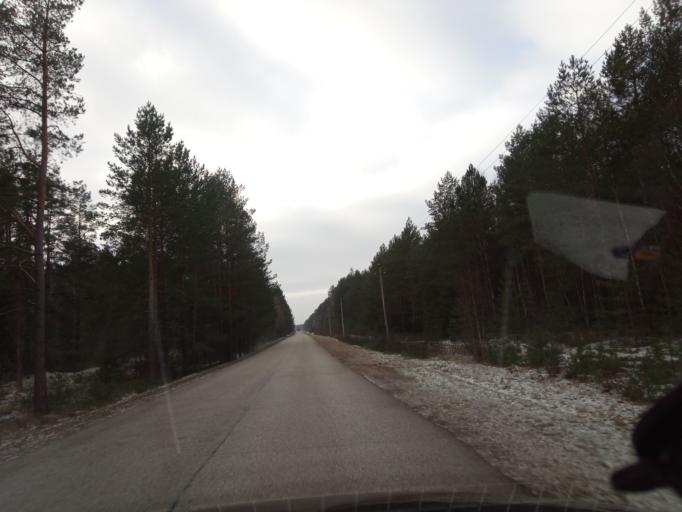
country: LT
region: Alytaus apskritis
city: Varena
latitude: 54.0350
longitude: 24.3668
